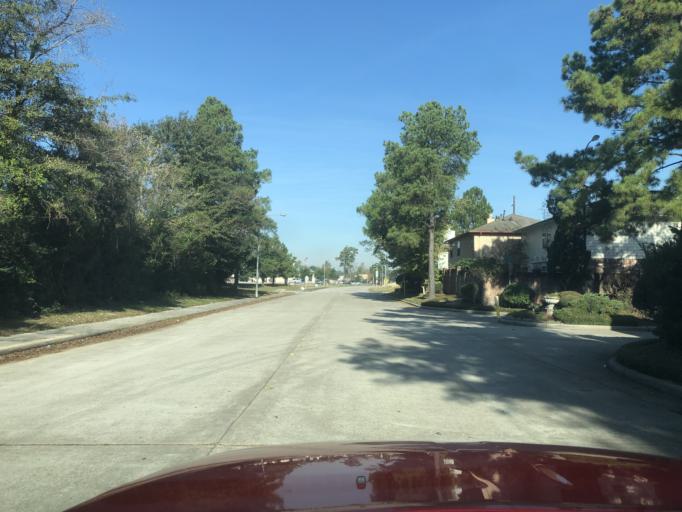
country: US
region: Texas
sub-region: Harris County
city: Spring
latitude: 30.0058
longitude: -95.4569
